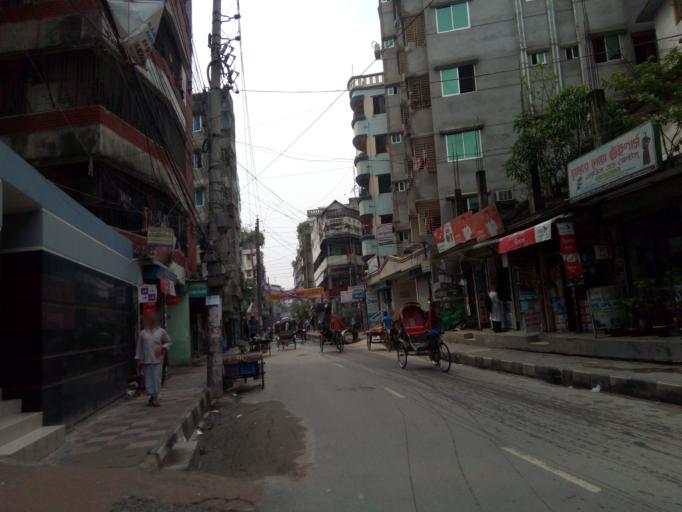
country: BD
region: Dhaka
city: Azimpur
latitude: 23.7410
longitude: 90.3705
